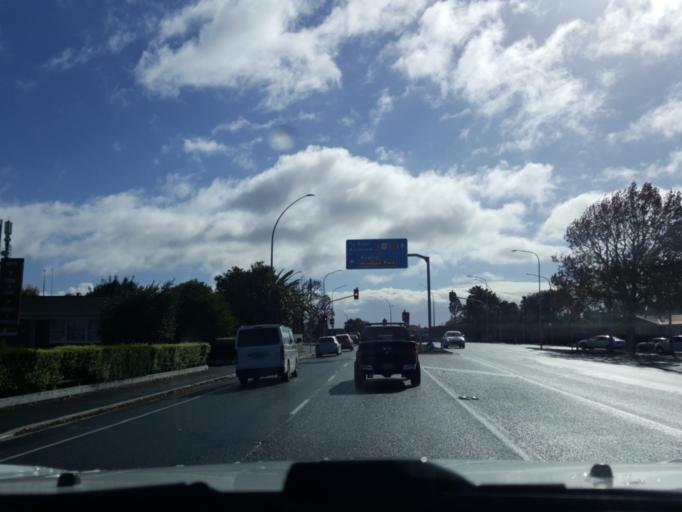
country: NZ
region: Waikato
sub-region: Hamilton City
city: Hamilton
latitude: -37.7704
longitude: 175.2629
